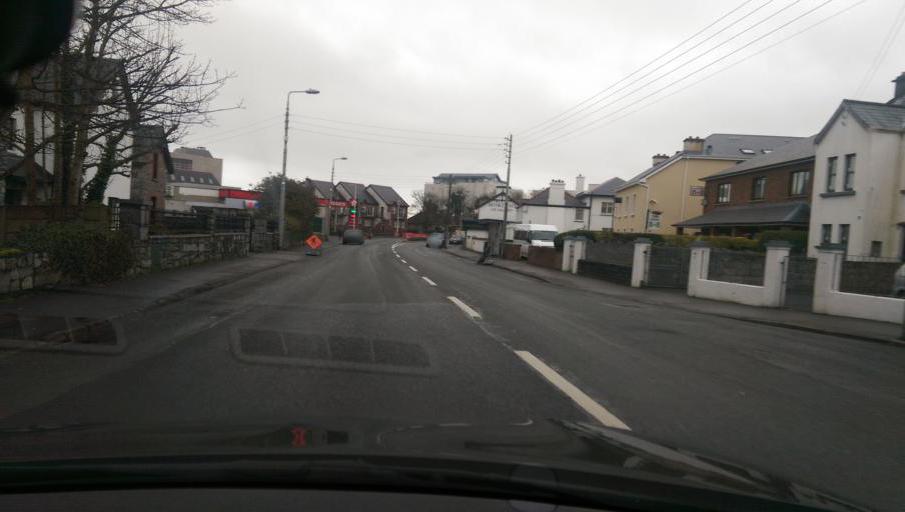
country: IE
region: Connaught
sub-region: County Galway
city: Gaillimh
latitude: 53.2641
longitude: -9.0725
